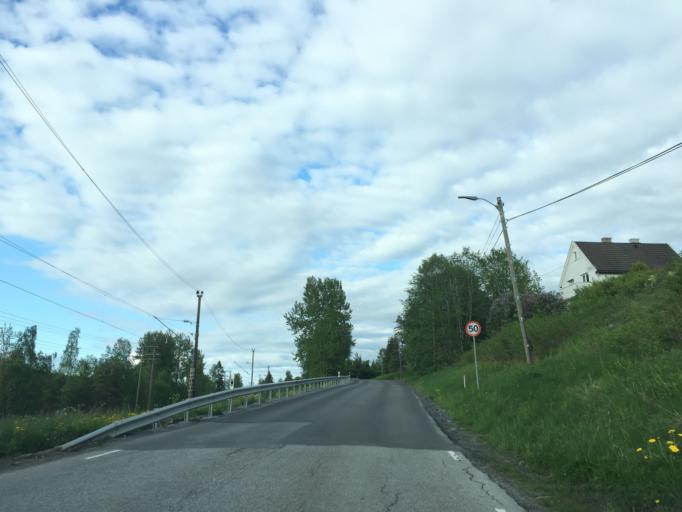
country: NO
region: Akershus
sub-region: Nes
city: Auli
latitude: 60.0301
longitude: 11.3300
